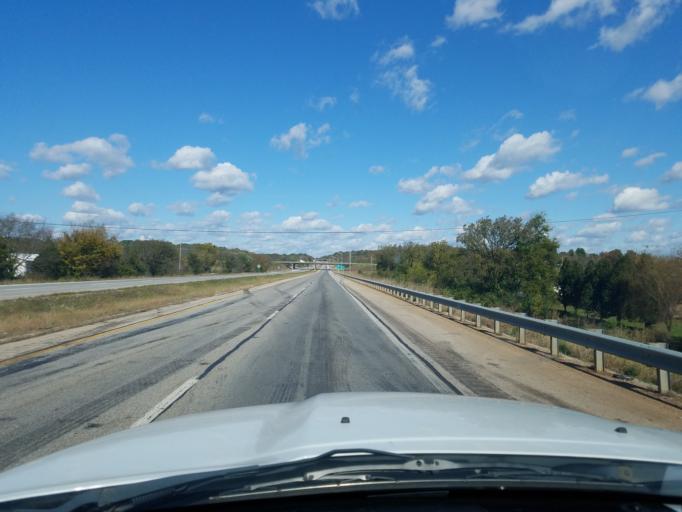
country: US
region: Kentucky
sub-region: Warren County
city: Bowling Green
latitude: 36.9877
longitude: -86.5028
